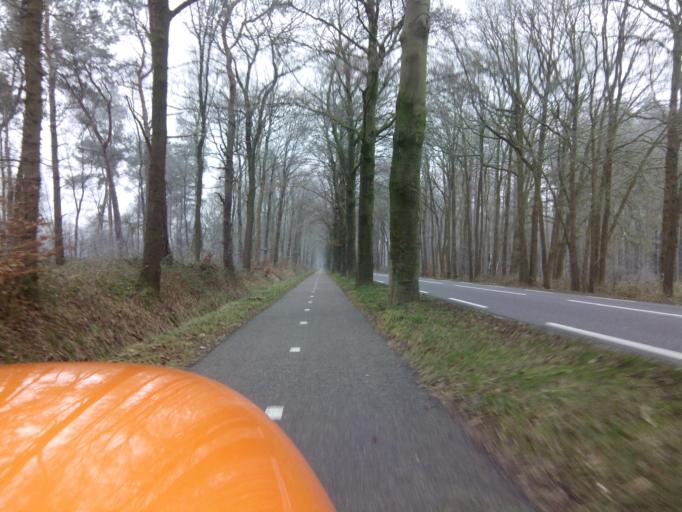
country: NL
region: Gelderland
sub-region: Gemeente Barneveld
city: Voorthuizen
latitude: 52.2077
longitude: 5.6080
